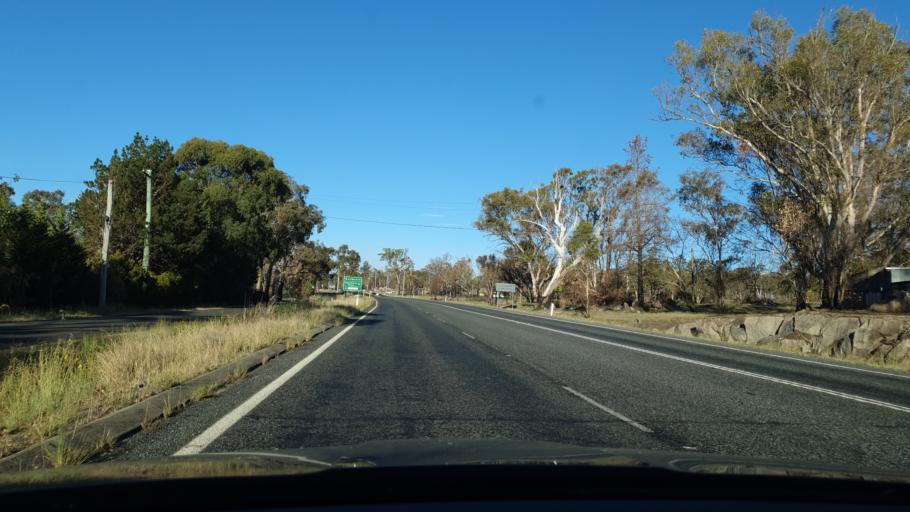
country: AU
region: Queensland
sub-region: Southern Downs
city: Stanthorpe
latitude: -28.6375
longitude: 151.9473
